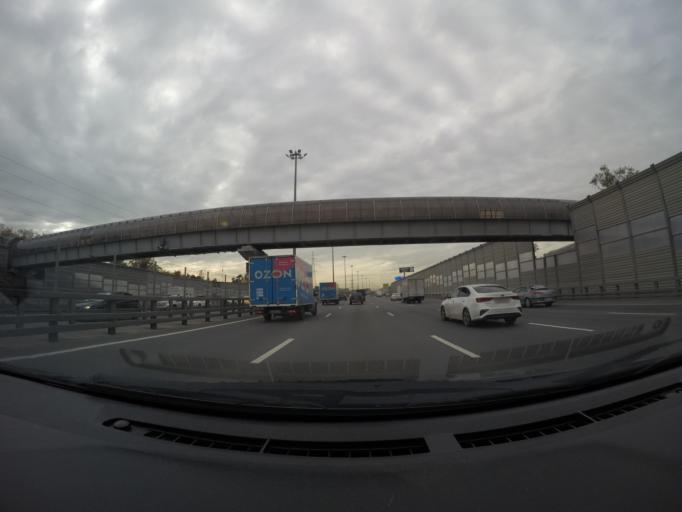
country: RU
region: Moskovskaya
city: Druzhba
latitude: 55.8892
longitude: 37.7391
